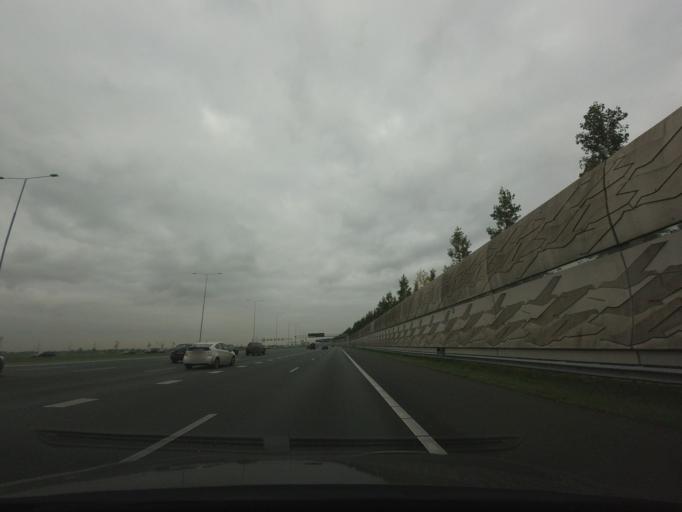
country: NL
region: North Holland
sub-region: Gemeente Amsterdam
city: Amsterdam-Zuidoost
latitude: 52.2700
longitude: 4.9605
